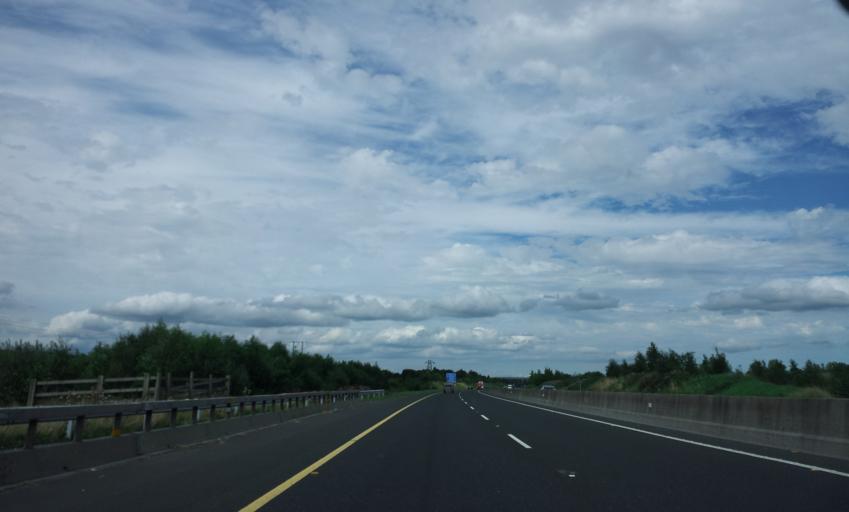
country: IE
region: Leinster
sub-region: Kildare
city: Old Kilcullen
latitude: 53.0945
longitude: -6.7531
